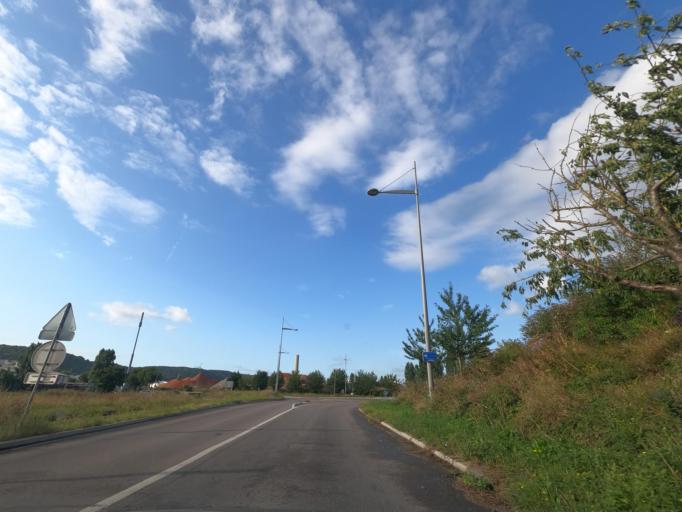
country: FR
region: Haute-Normandie
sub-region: Departement de la Seine-Maritime
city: Petit-Couronne
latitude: 49.3996
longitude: 1.0194
